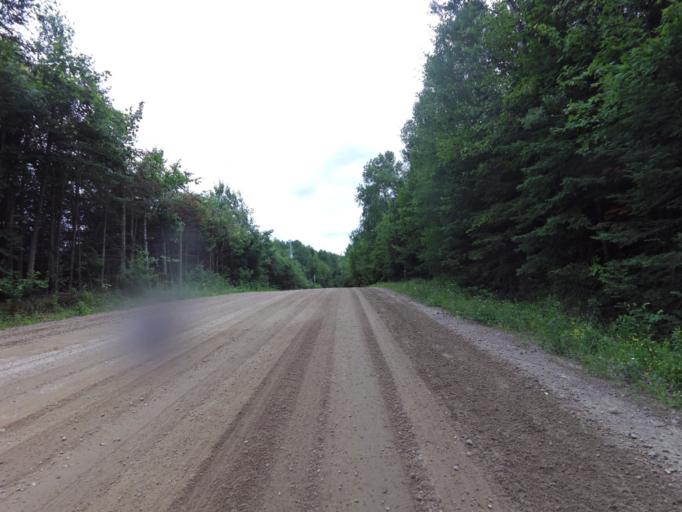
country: CA
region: Quebec
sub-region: Laurentides
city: Mont-Tremblant
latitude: 45.9435
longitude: -74.6476
